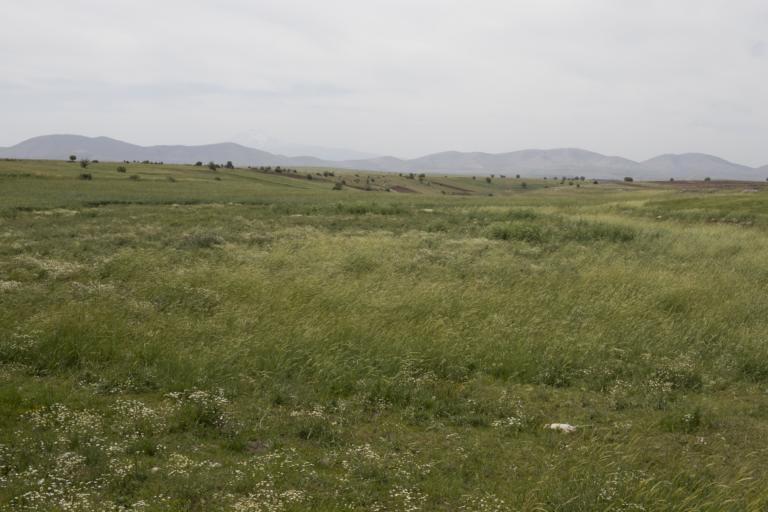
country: TR
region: Kayseri
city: Toklar
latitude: 38.4191
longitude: 36.0837
